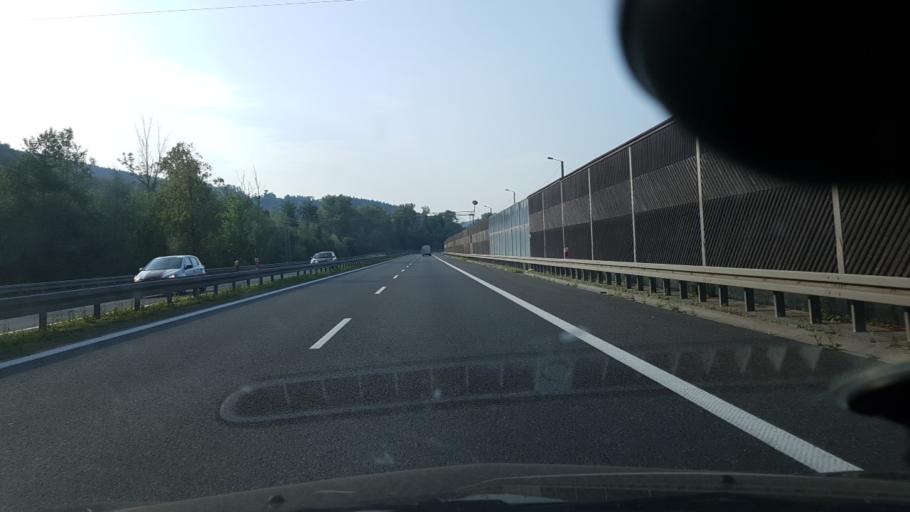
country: PL
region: Lesser Poland Voivodeship
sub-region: Powiat myslenicki
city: Stroza
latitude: 49.8088
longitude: 19.9231
